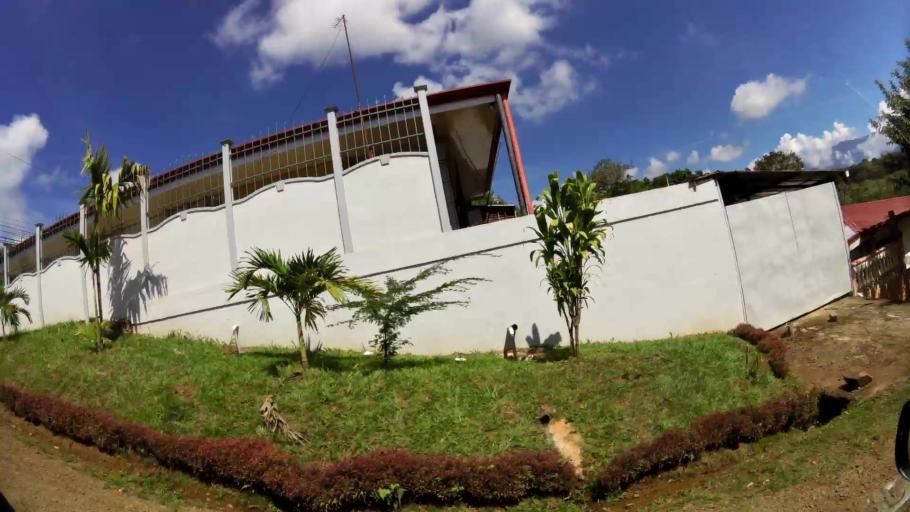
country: CR
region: San Jose
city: San Isidro
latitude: 9.3862
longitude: -83.7041
